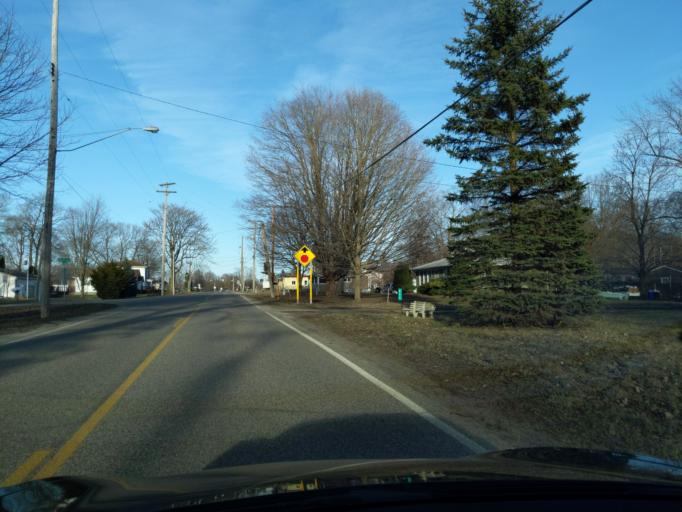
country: US
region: Michigan
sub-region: Ionia County
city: Ionia
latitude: 42.9680
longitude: -85.0723
